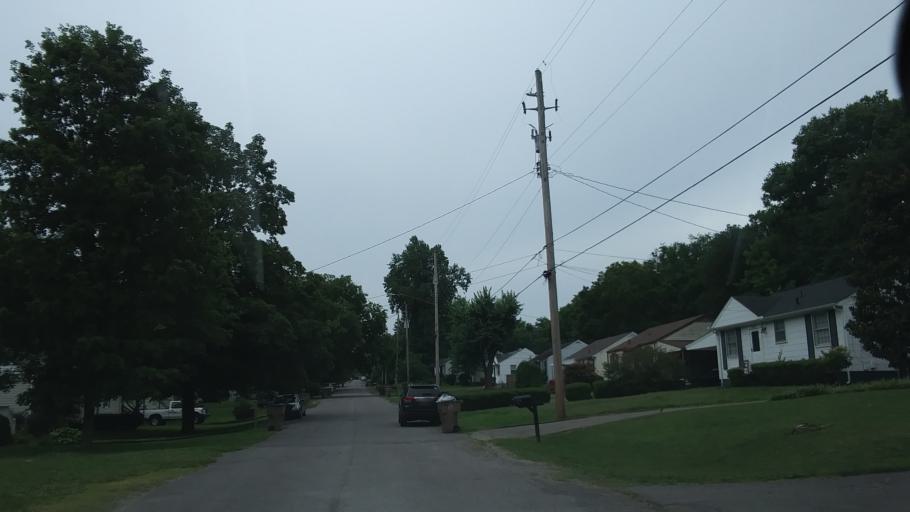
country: US
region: Tennessee
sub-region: Davidson County
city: Belle Meade
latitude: 36.1444
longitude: -86.8536
